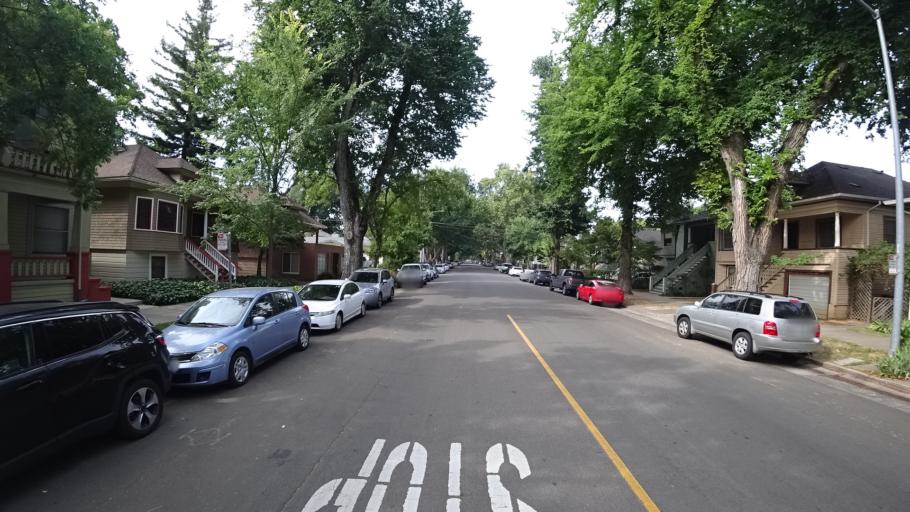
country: US
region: California
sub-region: Sacramento County
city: Sacramento
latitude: 38.5835
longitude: -121.4785
